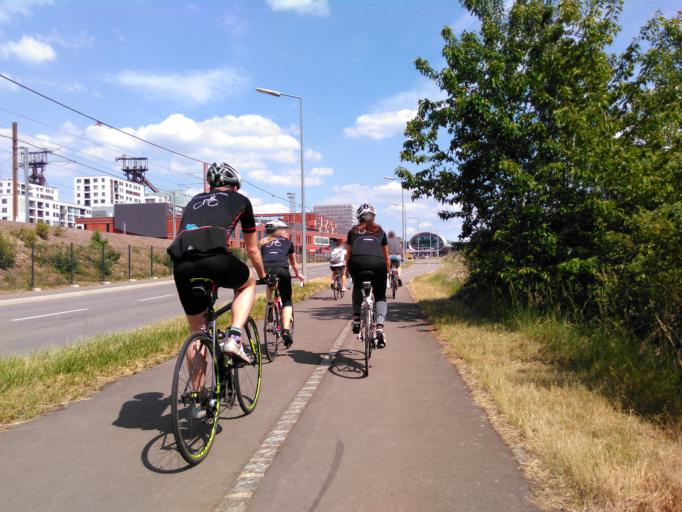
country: LU
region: Luxembourg
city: Belvaux
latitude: 49.5008
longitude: 5.9417
